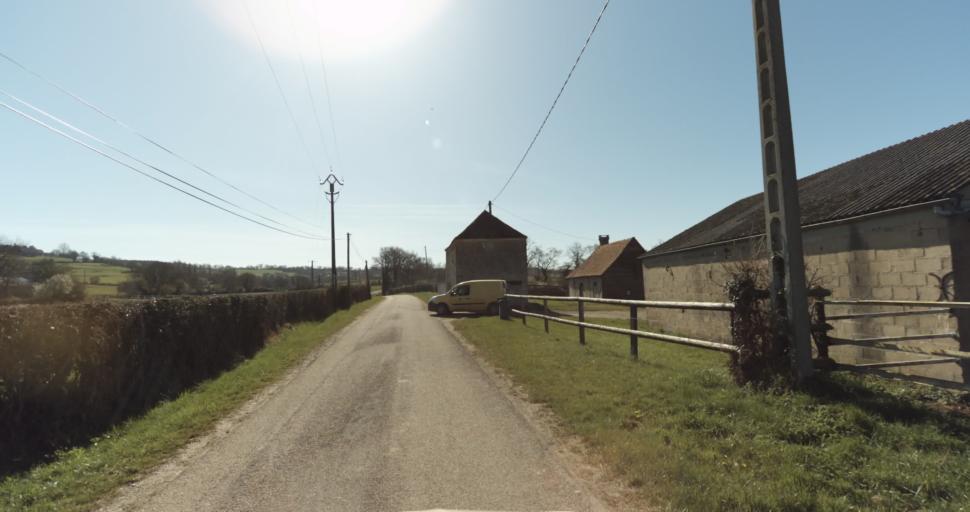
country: FR
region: Lower Normandy
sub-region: Departement de l'Orne
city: Trun
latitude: 48.9321
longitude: 0.0438
